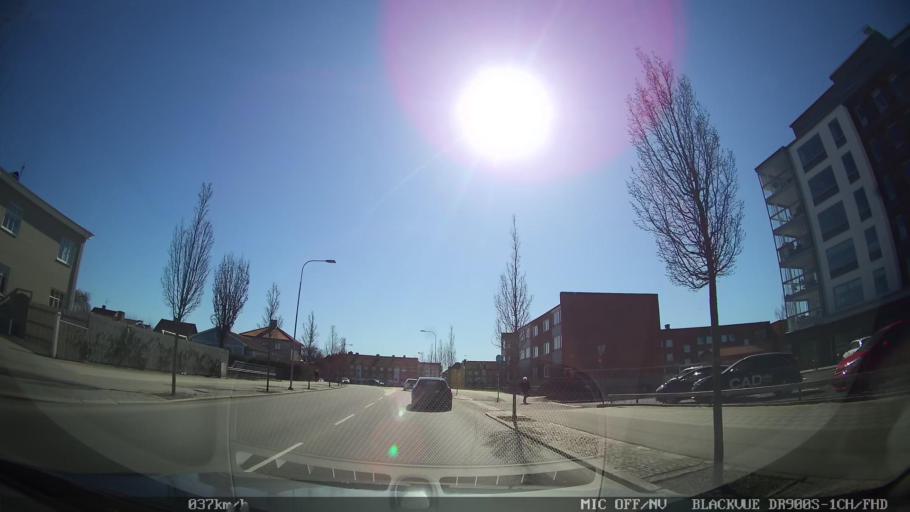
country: SE
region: Skane
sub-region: Ystads Kommun
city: Ystad
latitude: 55.4300
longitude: 13.8049
